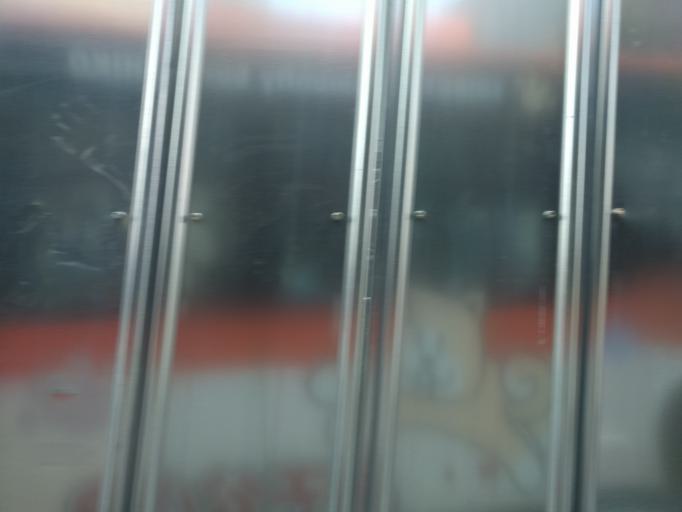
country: JP
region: Tokyo
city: Tokyo
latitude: 35.6832
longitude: 139.6744
